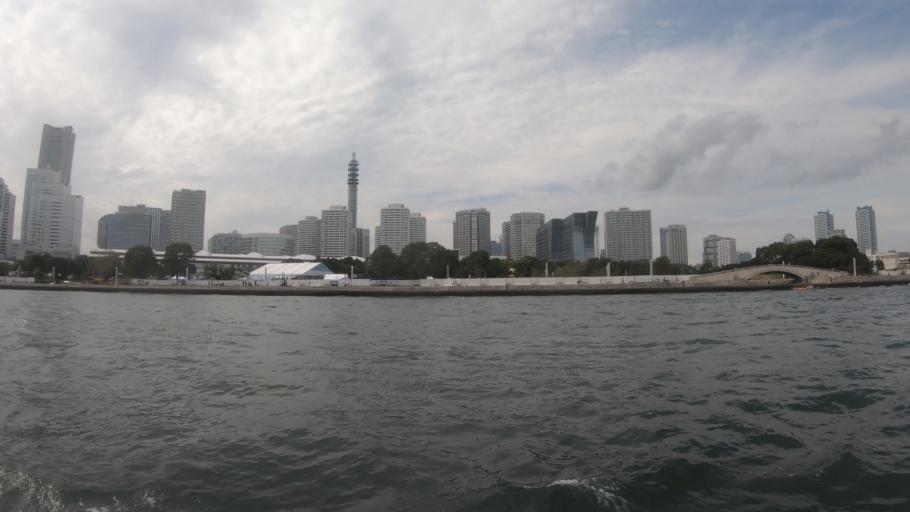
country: JP
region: Kanagawa
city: Yokohama
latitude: 35.4613
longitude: 139.6393
